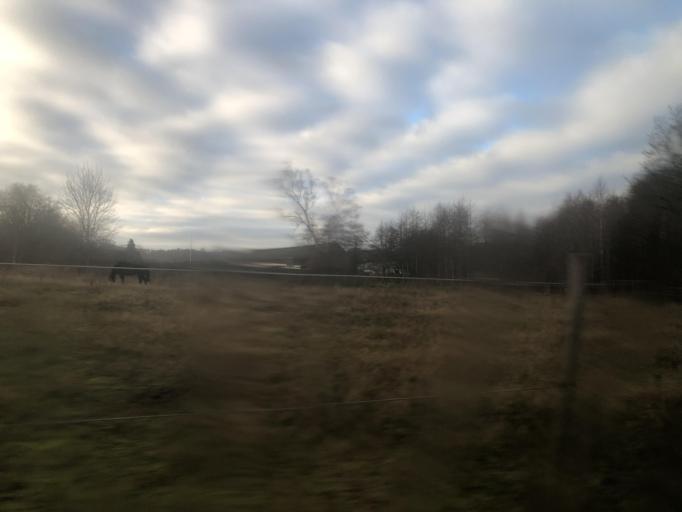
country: SE
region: Skane
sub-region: Lunds Kommun
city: Veberod
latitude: 55.6049
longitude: 13.5373
